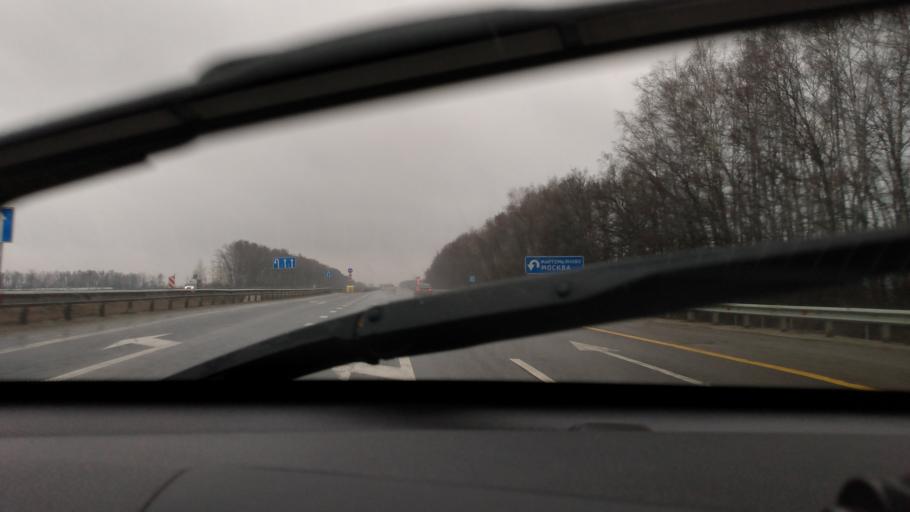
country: RU
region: Moskovskaya
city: Ozherel'ye
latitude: 54.6325
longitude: 38.1604
